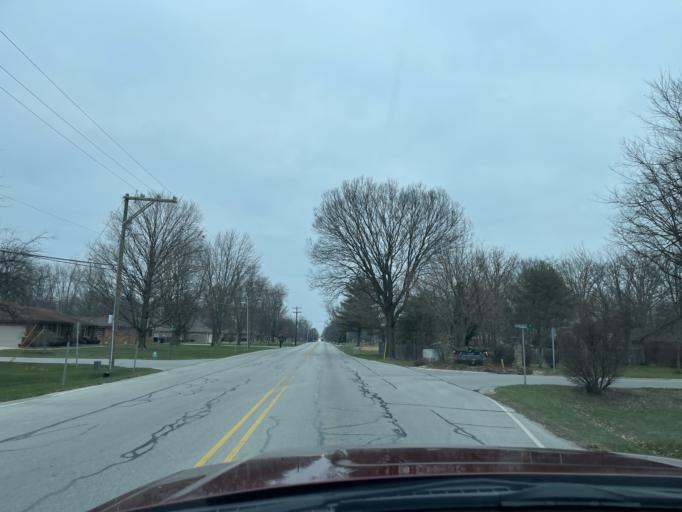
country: US
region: Indiana
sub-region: Hendricks County
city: Avon
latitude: 39.7861
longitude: -86.4003
